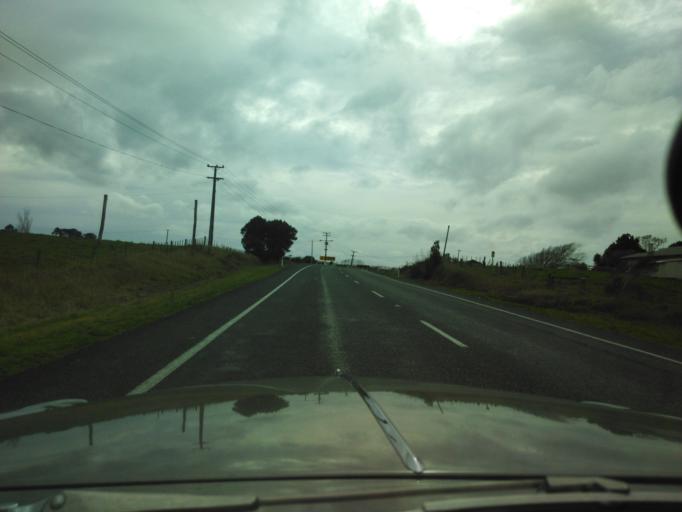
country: NZ
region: Auckland
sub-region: Auckland
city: Parakai
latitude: -36.6958
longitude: 174.4300
